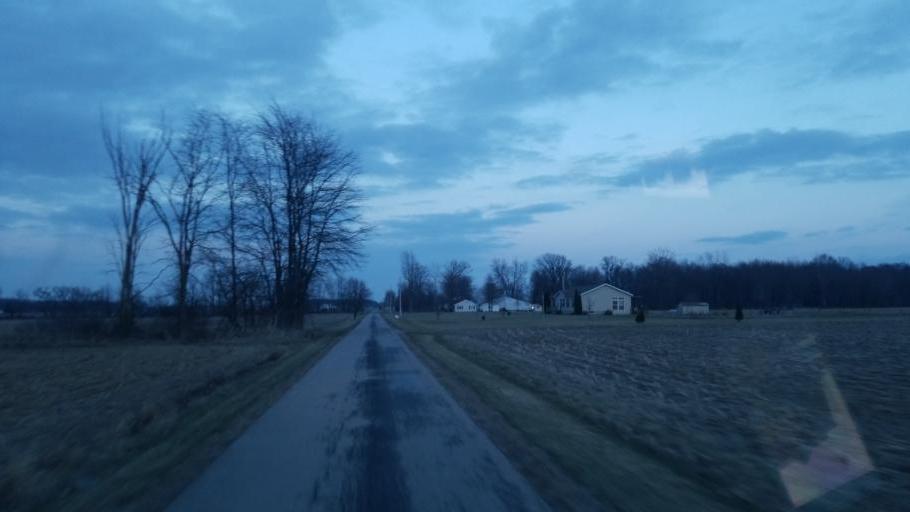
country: US
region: Ohio
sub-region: Morrow County
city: Cardington
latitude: 40.5724
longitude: -82.9485
